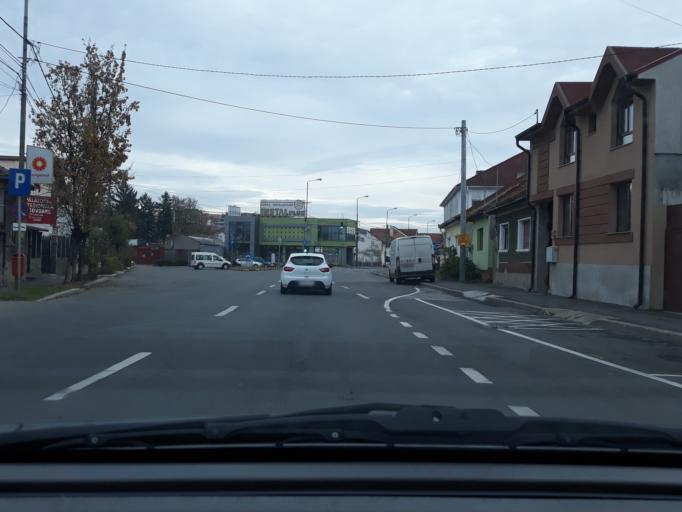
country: RO
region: Bihor
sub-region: Comuna Biharea
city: Oradea
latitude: 47.0493
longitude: 21.9542
